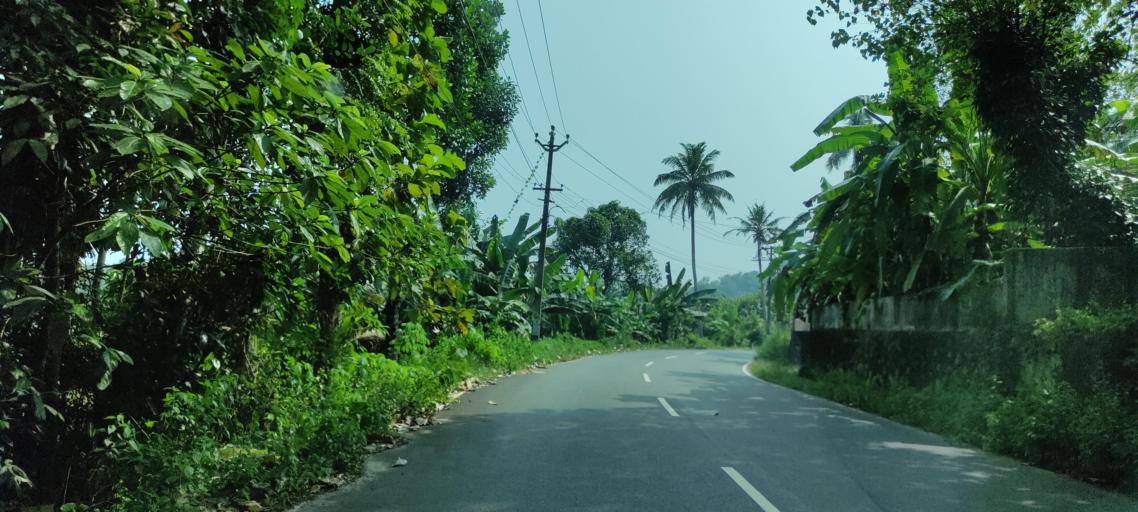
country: IN
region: Kerala
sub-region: Pattanamtitta
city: Adur
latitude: 9.2345
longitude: 76.6975
